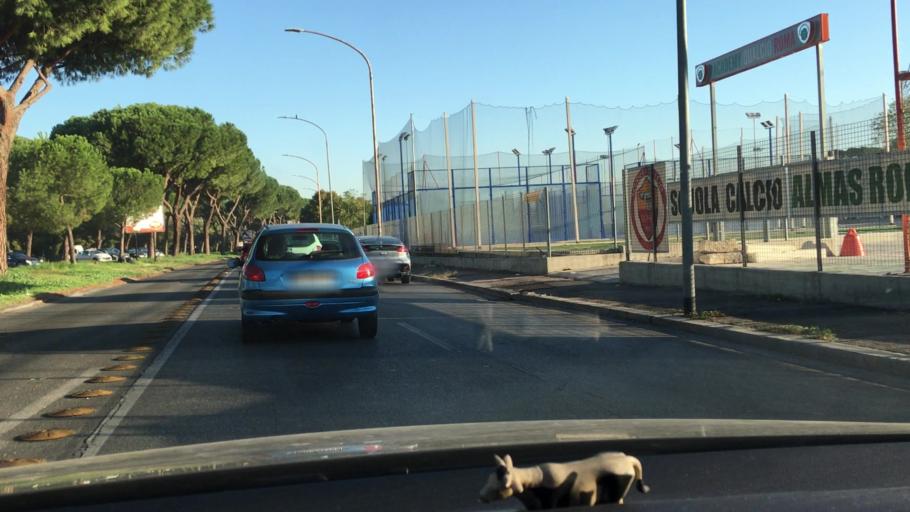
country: IT
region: Latium
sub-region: Citta metropolitana di Roma Capitale
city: Rome
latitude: 41.8706
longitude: 12.5685
